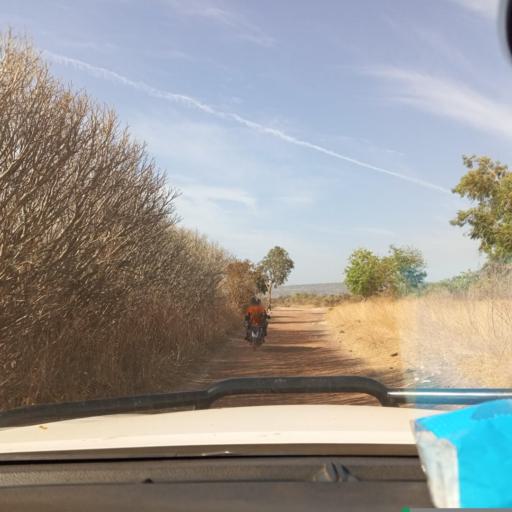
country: ML
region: Bamako
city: Bamako
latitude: 12.5577
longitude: -8.1356
